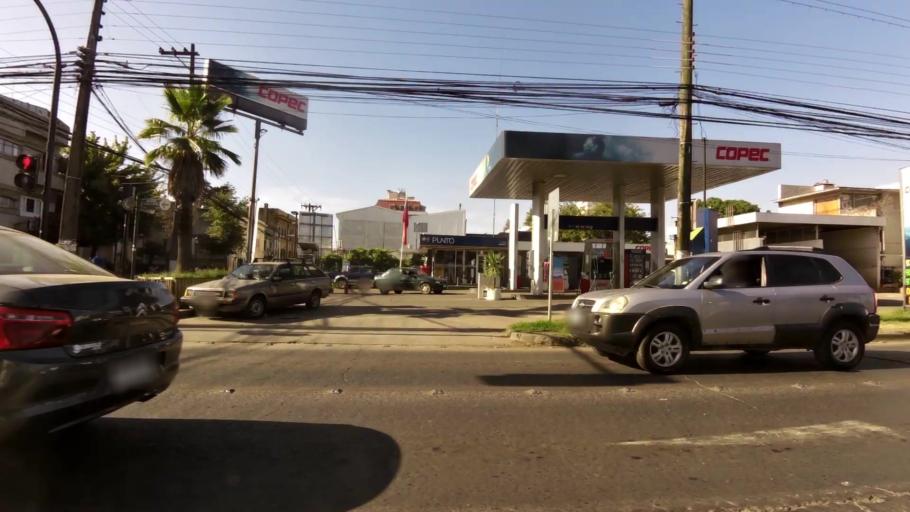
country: CL
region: Maule
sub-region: Provincia de Talca
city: Talca
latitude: -35.4283
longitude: -71.6653
